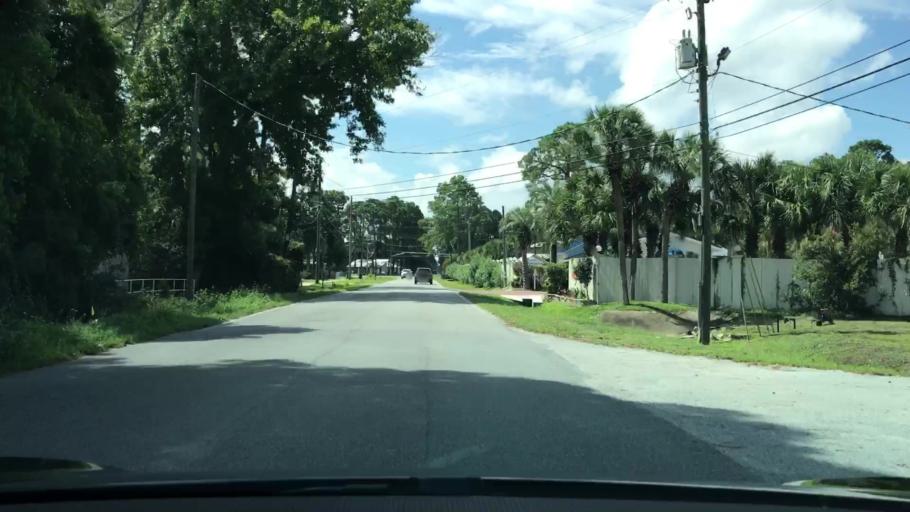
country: US
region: Florida
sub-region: Bay County
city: Panama City Beach
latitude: 30.1843
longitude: -85.7866
